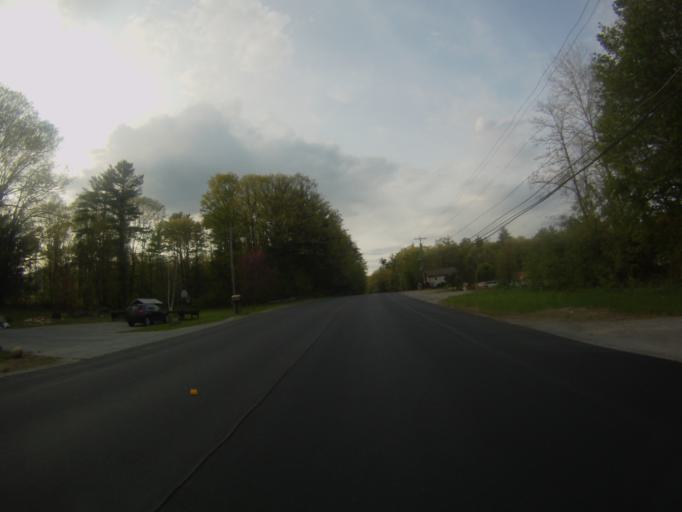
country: US
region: New York
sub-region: Essex County
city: Ticonderoga
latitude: 43.8061
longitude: -73.4883
